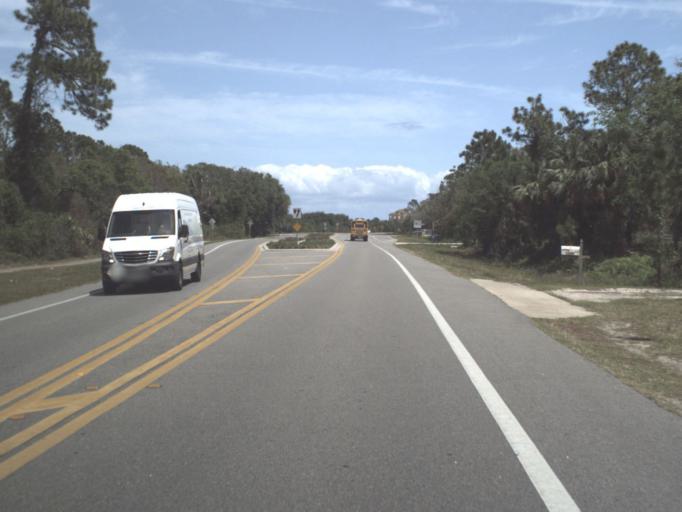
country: US
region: Florida
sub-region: Flagler County
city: Palm Coast
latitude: 29.5631
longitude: -81.1765
